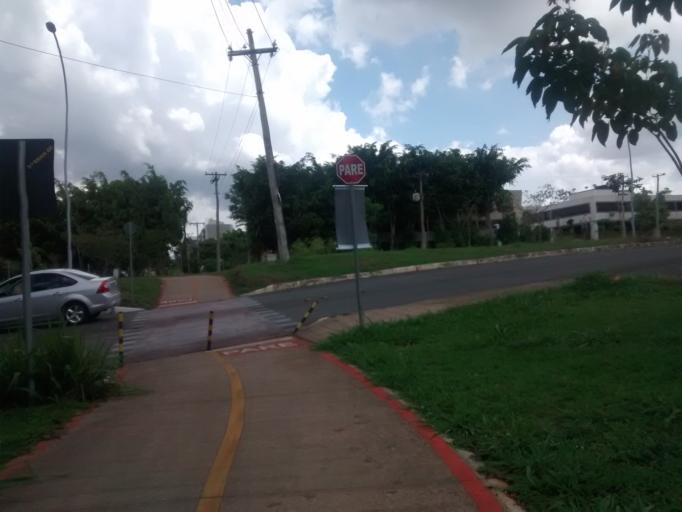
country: BR
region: Federal District
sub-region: Brasilia
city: Brasilia
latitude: -15.7500
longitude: -47.8846
